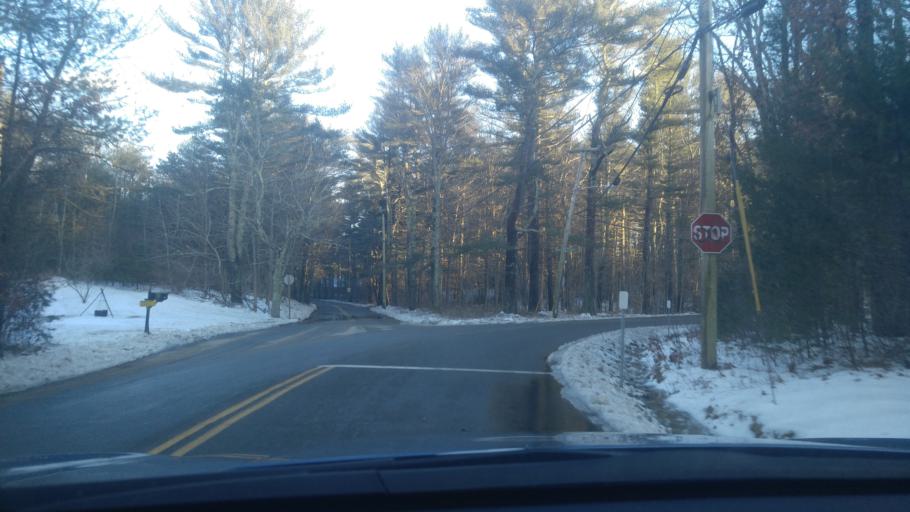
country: US
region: Rhode Island
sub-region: Kent County
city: Coventry
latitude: 41.7188
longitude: -71.6535
